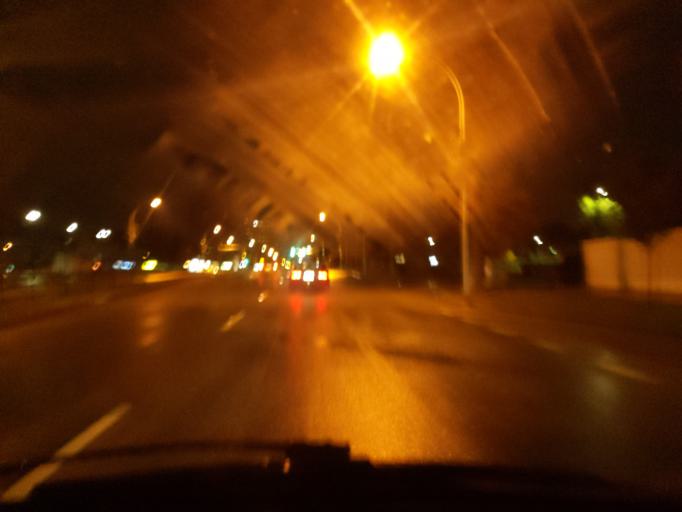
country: CA
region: British Columbia
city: Surrey
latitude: 49.1916
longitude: -122.8041
